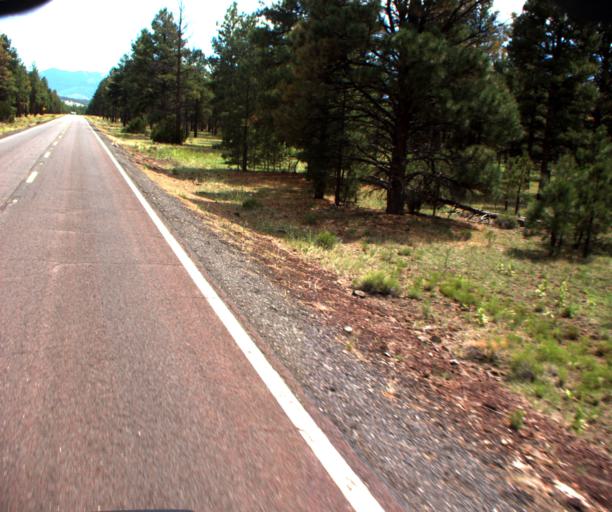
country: US
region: Arizona
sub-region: Coconino County
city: Parks
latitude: 35.4670
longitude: -111.7858
